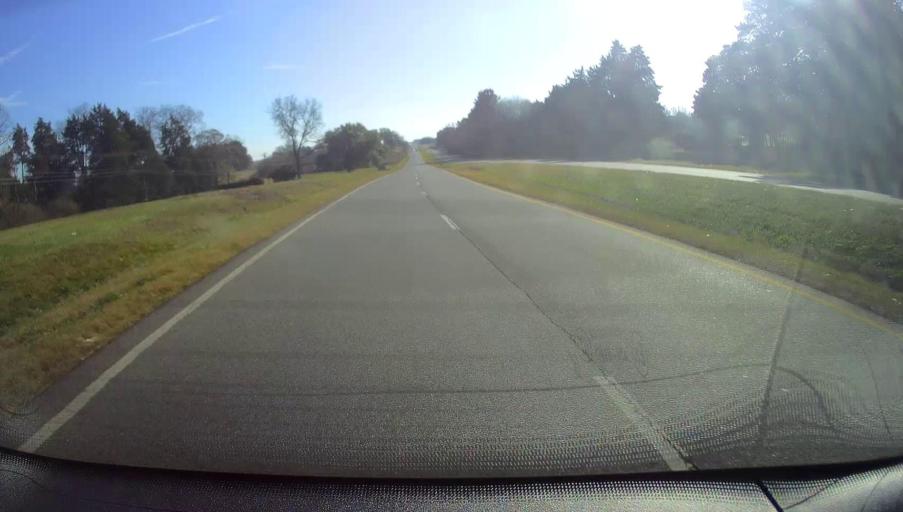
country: US
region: Alabama
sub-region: Morgan County
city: Decatur
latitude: 34.6803
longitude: -86.9496
